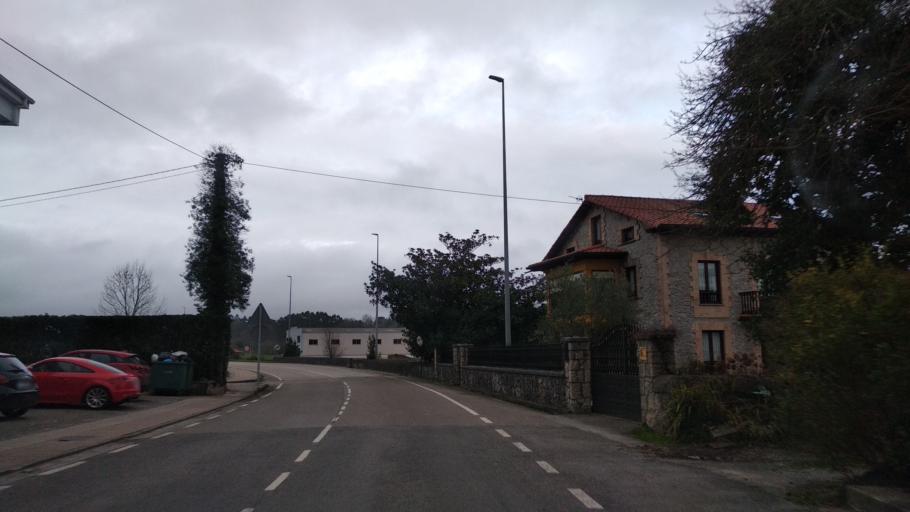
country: ES
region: Cantabria
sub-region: Provincia de Cantabria
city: Entrambasaguas
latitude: 43.4132
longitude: -3.6982
